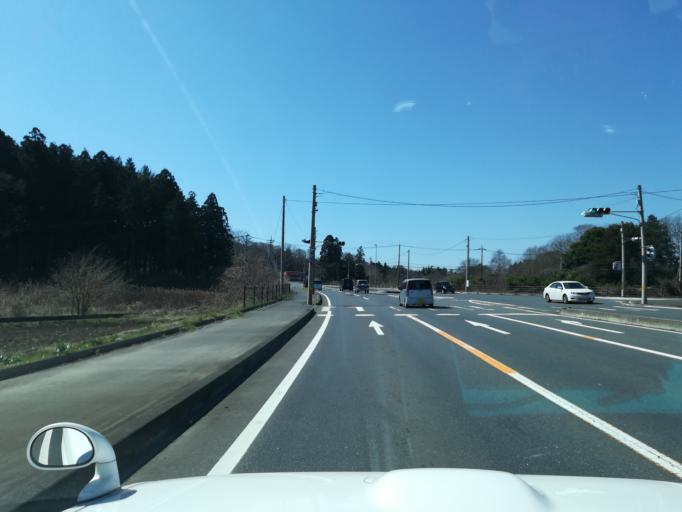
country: JP
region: Ibaraki
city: Ushiku
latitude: 35.9682
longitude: 140.1723
